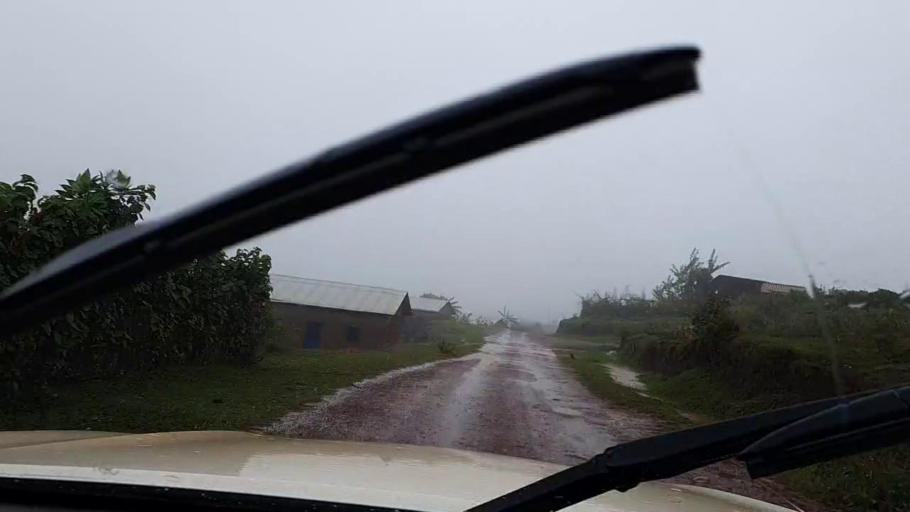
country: RW
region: Northern Province
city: Byumba
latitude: -1.7356
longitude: 30.0119
